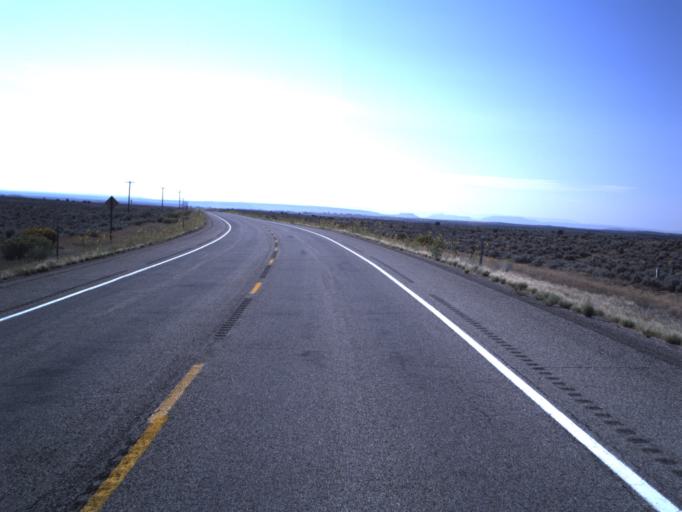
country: US
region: Utah
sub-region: San Juan County
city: Blanding
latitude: 37.5134
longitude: -109.4935
